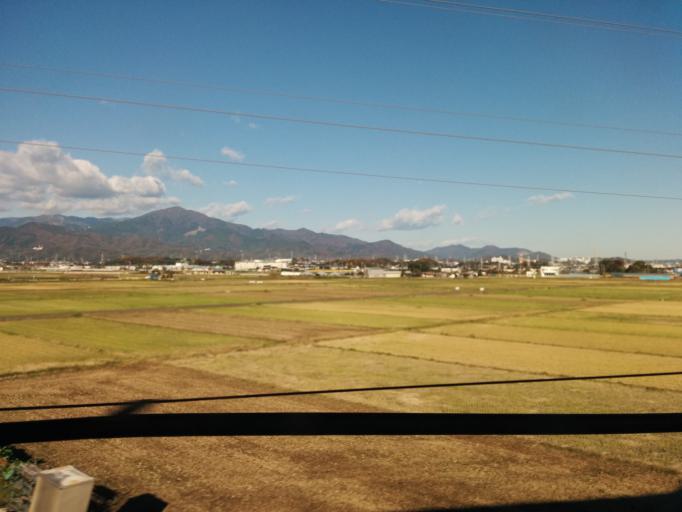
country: JP
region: Kanagawa
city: Isehara
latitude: 35.3636
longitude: 139.3314
